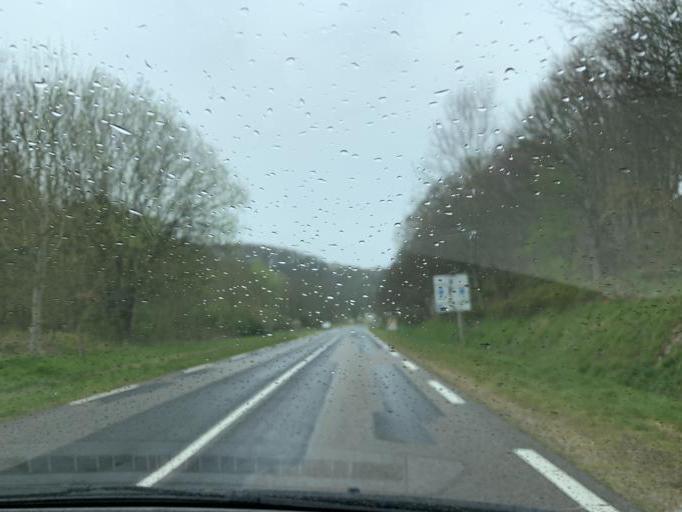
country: FR
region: Haute-Normandie
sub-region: Departement de la Seine-Maritime
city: Etretat
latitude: 49.6990
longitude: 0.2014
